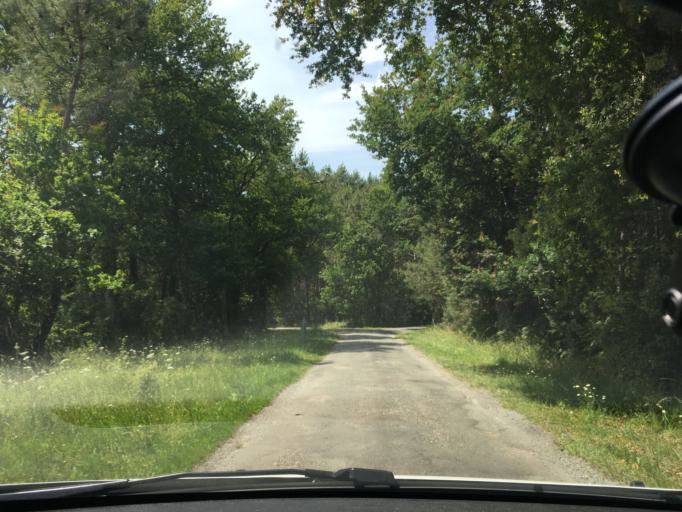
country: FR
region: Aquitaine
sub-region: Departement de la Gironde
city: Lesparre-Medoc
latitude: 45.2801
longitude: -0.9061
